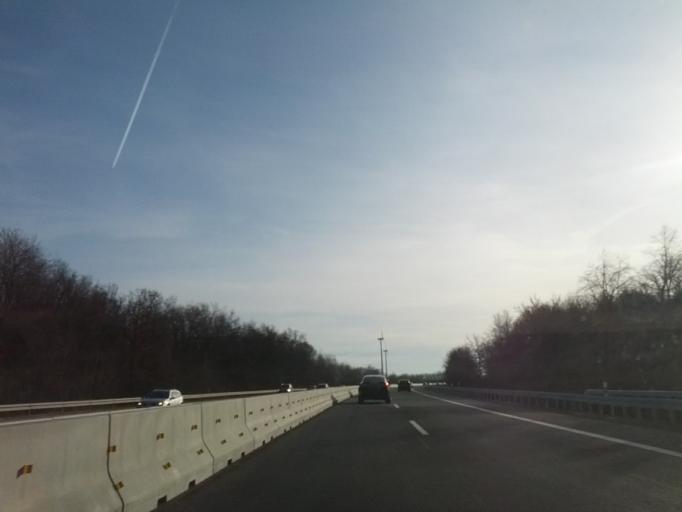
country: DE
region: Bavaria
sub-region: Regierungsbezirk Mittelfranken
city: Gollhofen
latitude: 49.5291
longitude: 10.1898
